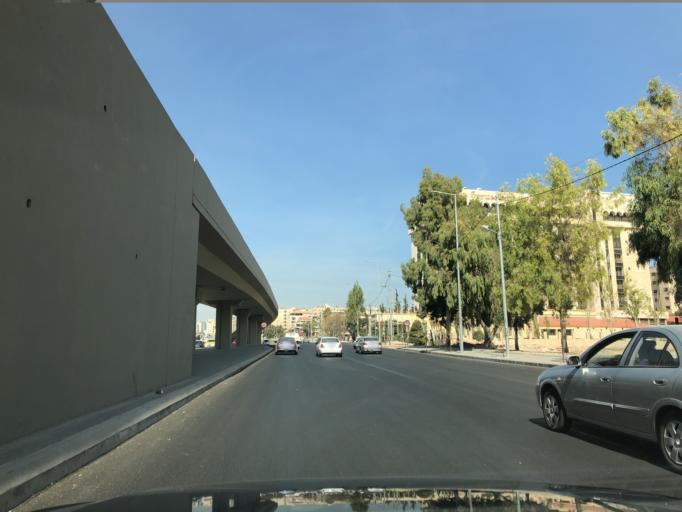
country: JO
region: Amman
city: Al Jubayhah
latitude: 31.9905
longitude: 35.8930
